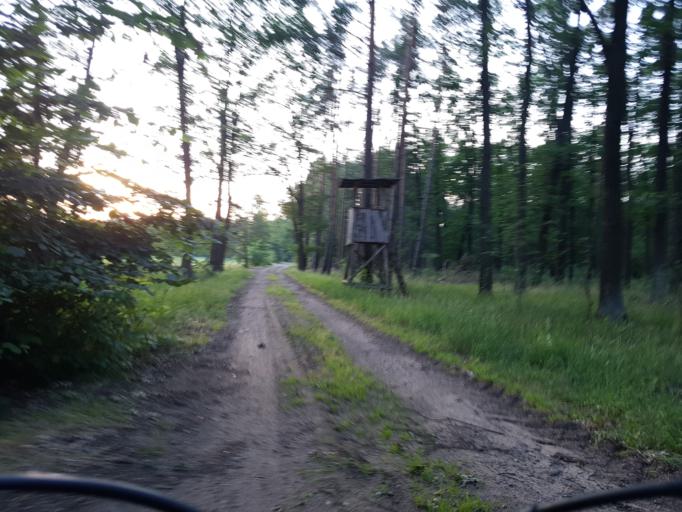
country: DE
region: Brandenburg
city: Schilda
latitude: 51.5847
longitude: 13.3454
